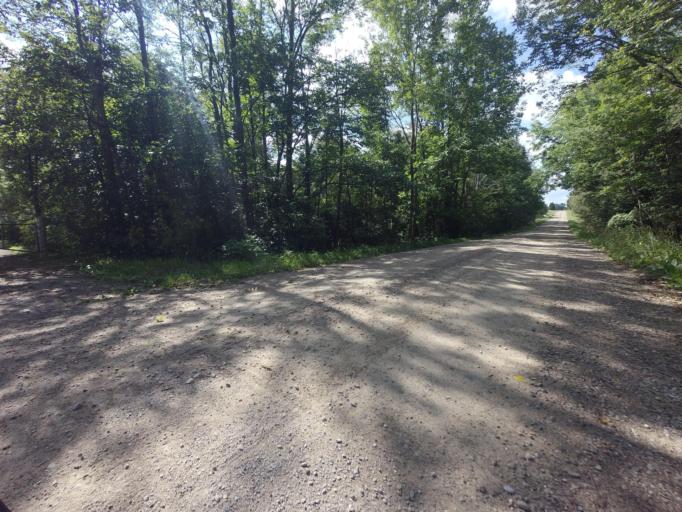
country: CA
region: Ontario
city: Huron East
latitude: 43.6894
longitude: -81.3218
